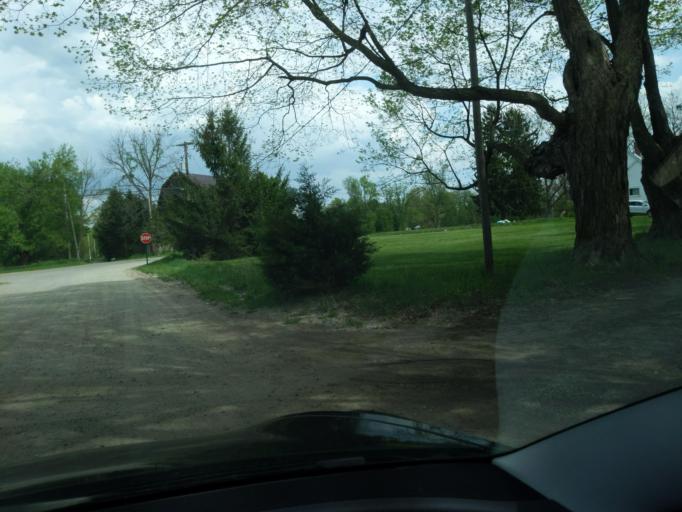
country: US
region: Michigan
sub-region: Livingston County
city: Pinckney
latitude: 42.4259
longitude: -84.0567
